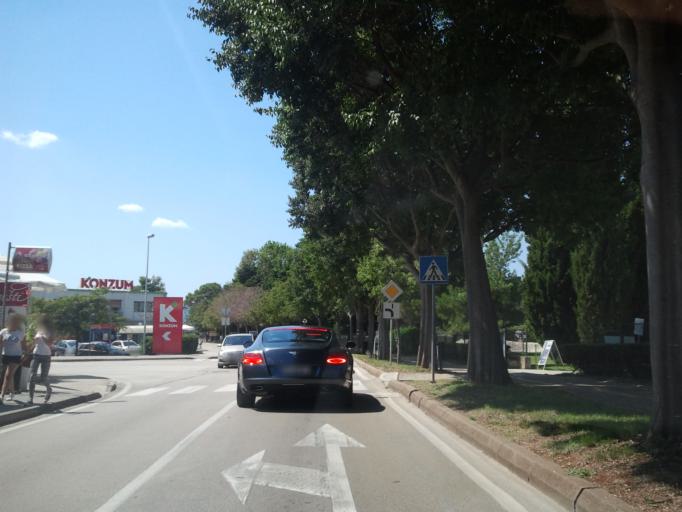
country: HR
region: Zadarska
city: Zadar
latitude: 44.1329
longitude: 15.2126
